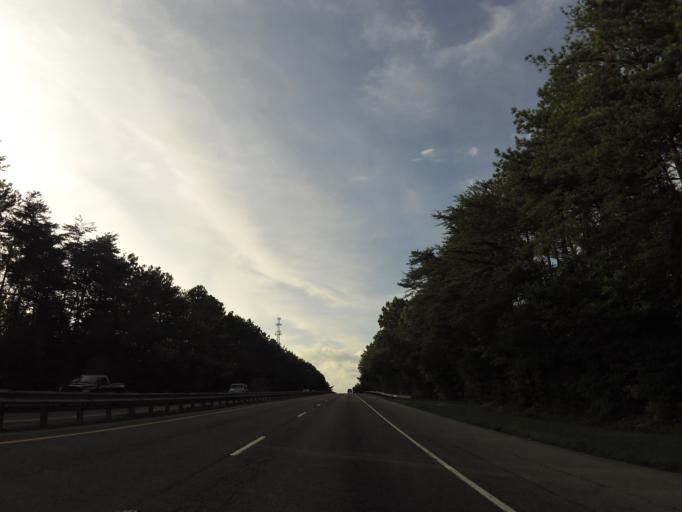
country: US
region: Tennessee
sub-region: Knox County
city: Farragut
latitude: 35.9692
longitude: -84.1767
